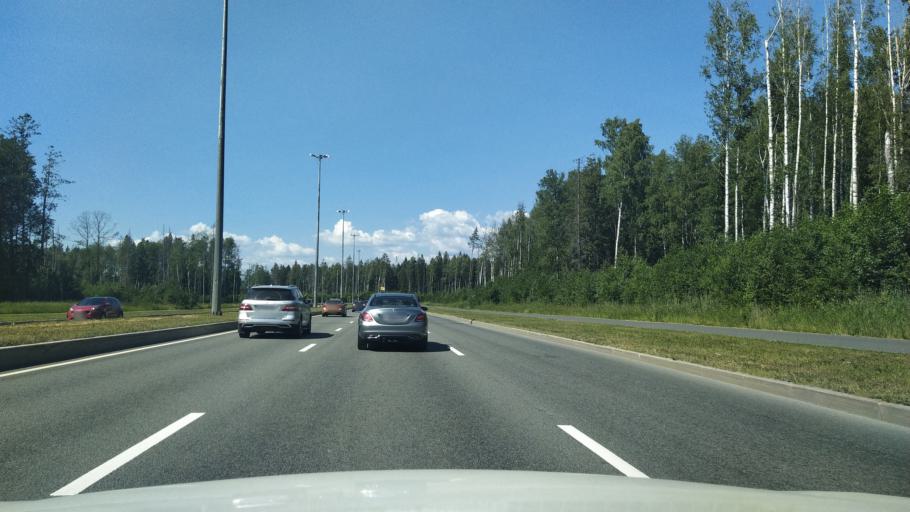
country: RU
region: St.-Petersburg
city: Levashovo
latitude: 60.0611
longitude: 30.2173
